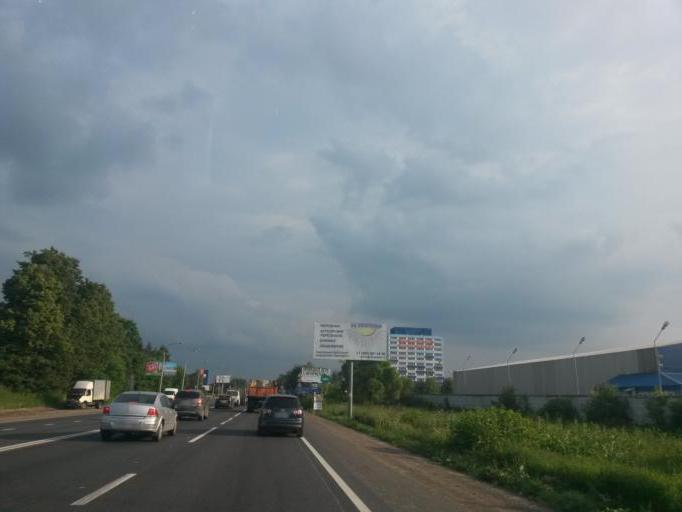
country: RU
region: Moskovskaya
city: Petrovskaya
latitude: 55.5508
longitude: 37.7745
